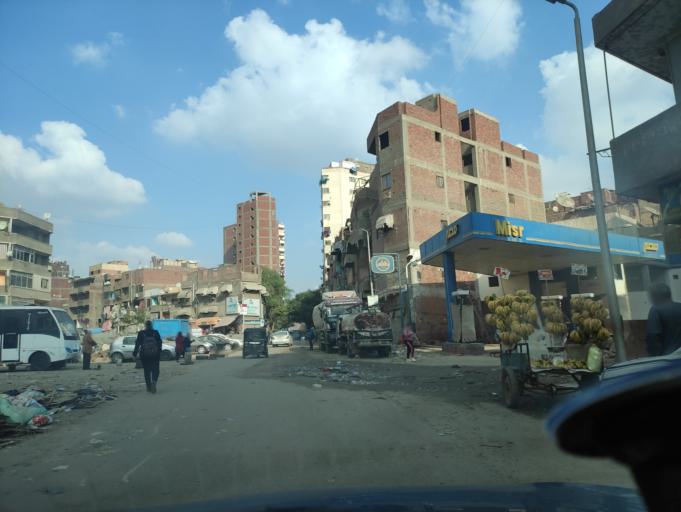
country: EG
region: Muhafazat al Qahirah
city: Cairo
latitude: 30.1249
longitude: 31.3041
